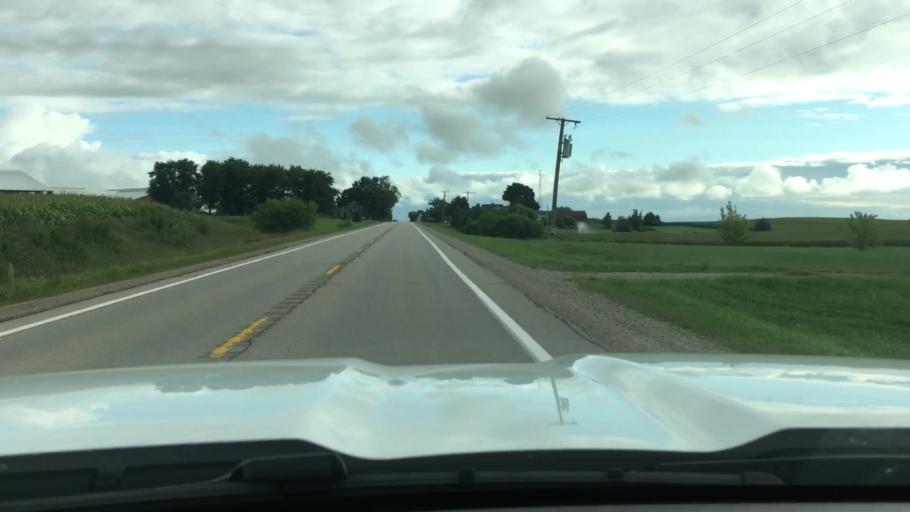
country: US
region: Michigan
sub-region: Tuscola County
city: Caro
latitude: 43.5492
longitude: -83.3274
